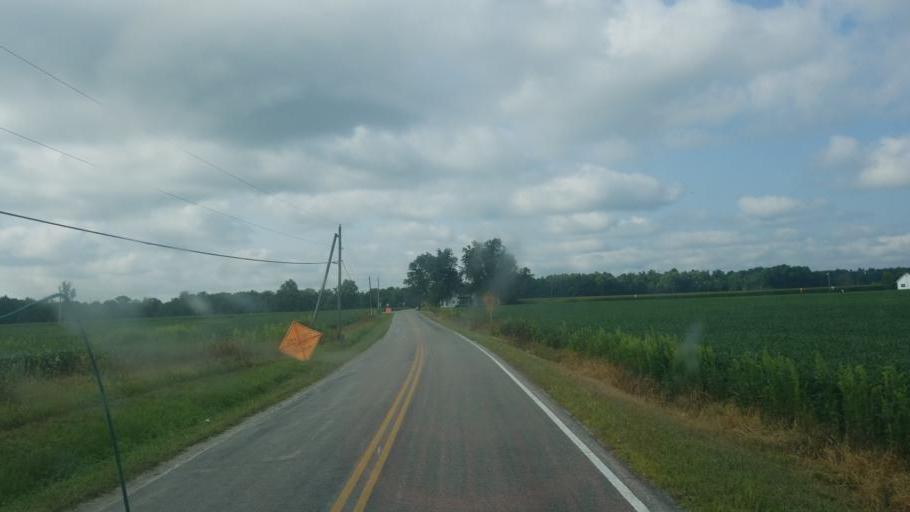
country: US
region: Ohio
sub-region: Morrow County
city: Cardington
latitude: 40.5639
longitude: -82.9975
